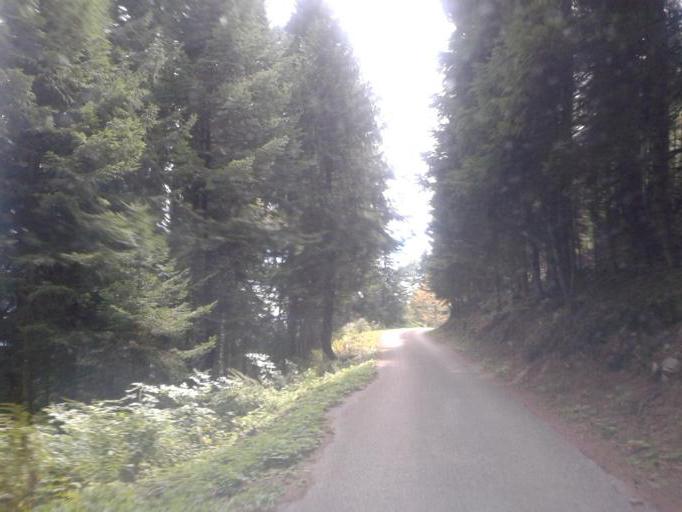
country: IT
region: Trentino-Alto Adige
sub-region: Provincia di Trento
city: Lodrone-Darzo
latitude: 45.8651
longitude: 10.5389
